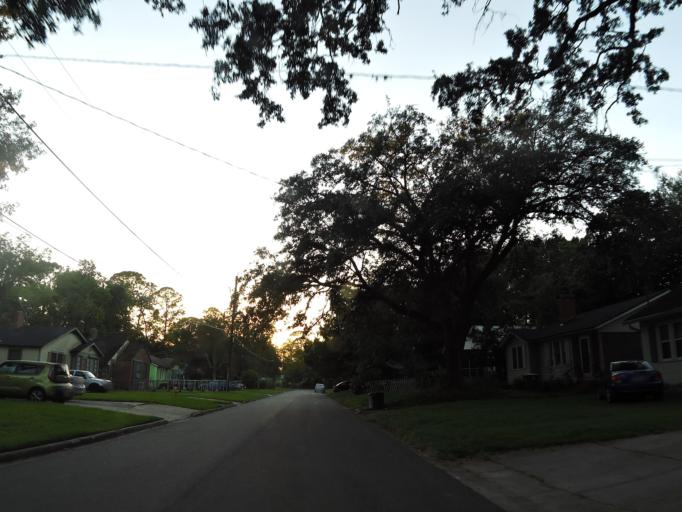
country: US
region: Florida
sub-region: Duval County
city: Jacksonville
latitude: 30.3154
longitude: -81.7184
